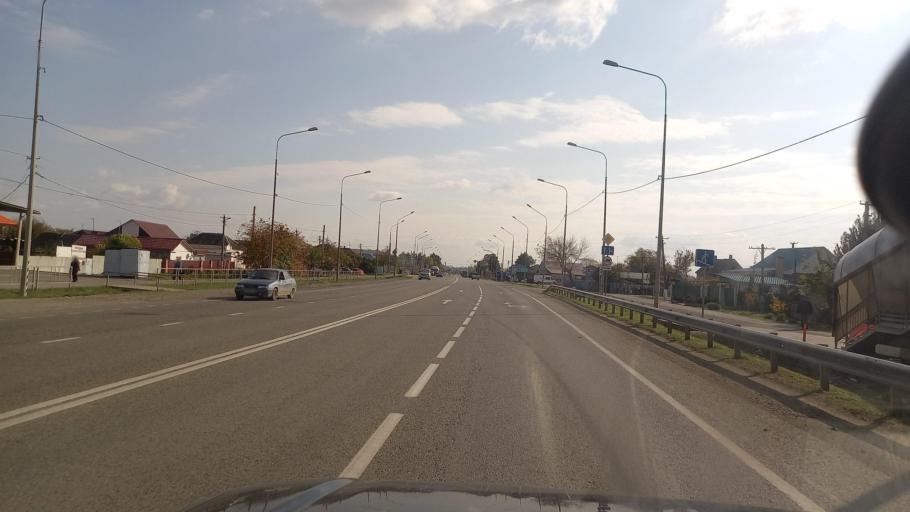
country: RU
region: Krasnodarskiy
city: Novoukrainskiy
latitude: 44.8963
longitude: 38.0505
